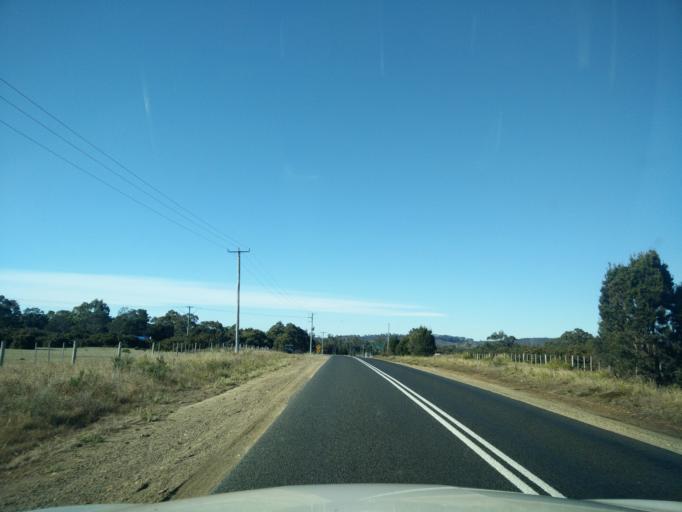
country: AU
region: Tasmania
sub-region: Break O'Day
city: St Helens
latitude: -41.9391
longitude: 148.2208
